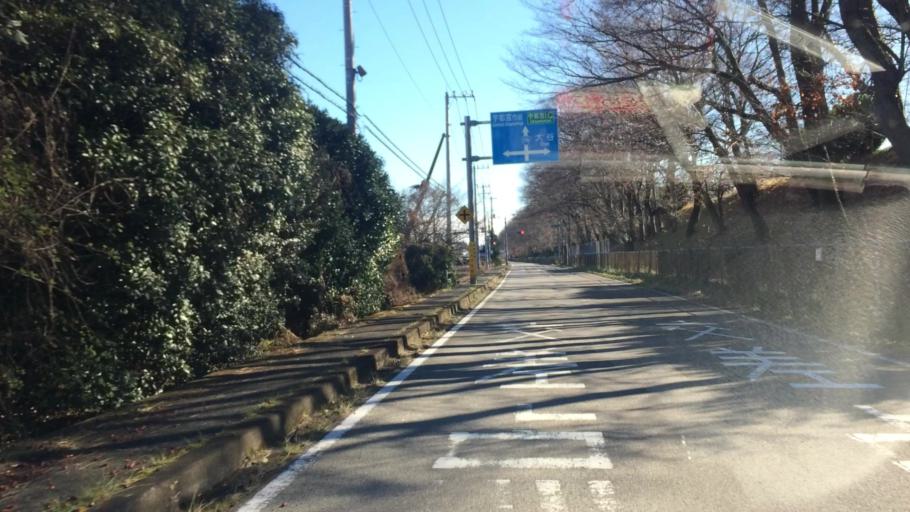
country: JP
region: Tochigi
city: Utsunomiya-shi
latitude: 36.6452
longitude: 139.8402
